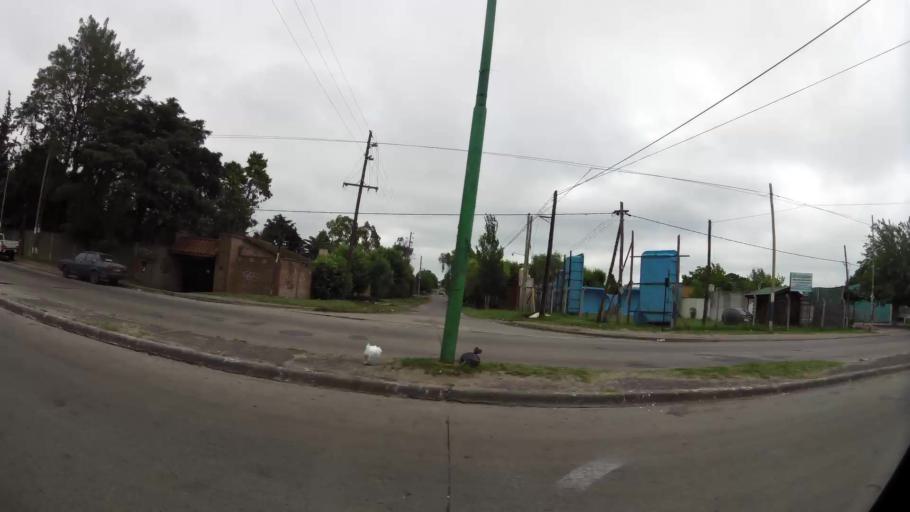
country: AR
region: Buenos Aires
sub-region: Partido de La Plata
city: La Plata
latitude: -34.9532
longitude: -58.0019
